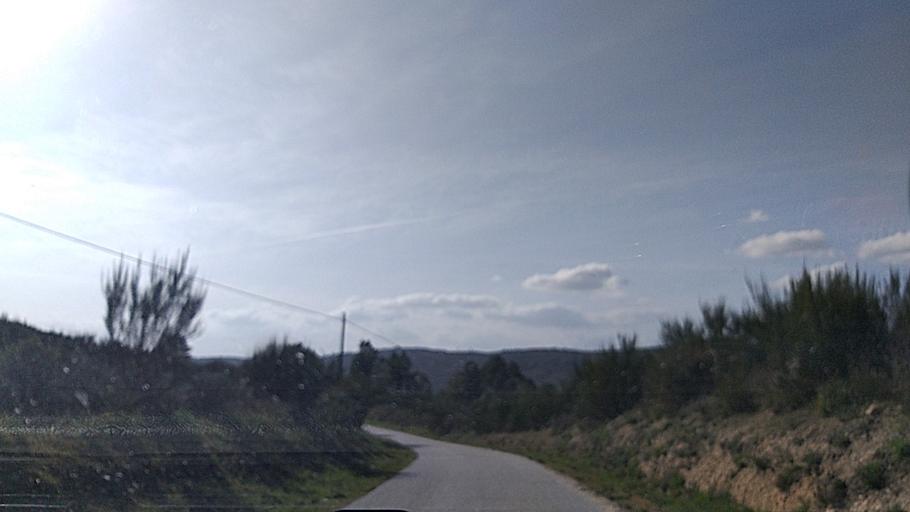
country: PT
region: Guarda
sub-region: Celorico da Beira
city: Celorico da Beira
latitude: 40.6547
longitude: -7.4027
